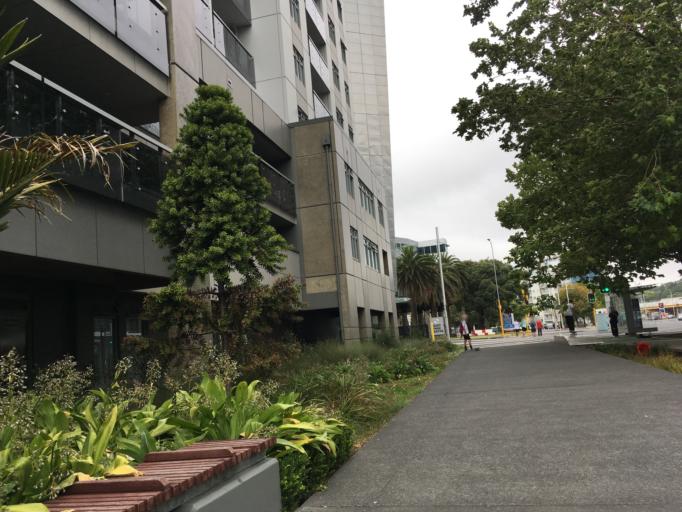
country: NZ
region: Auckland
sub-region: Auckland
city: Auckland
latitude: -36.8469
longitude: 174.7735
